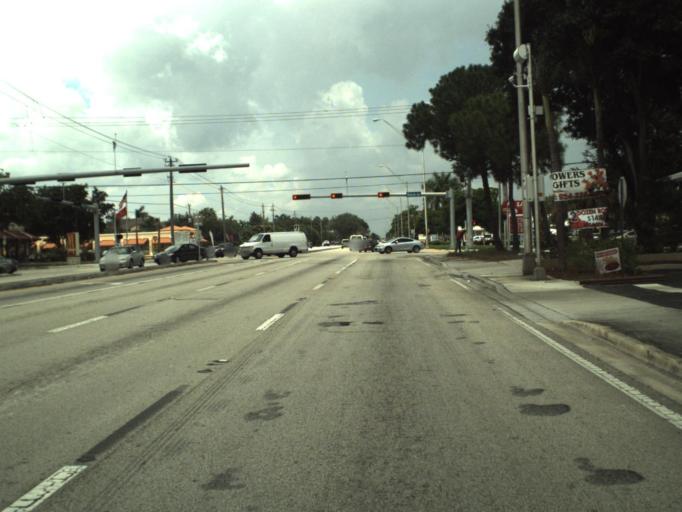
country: US
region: Florida
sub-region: Broward County
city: Davie
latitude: 26.0461
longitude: -80.2306
